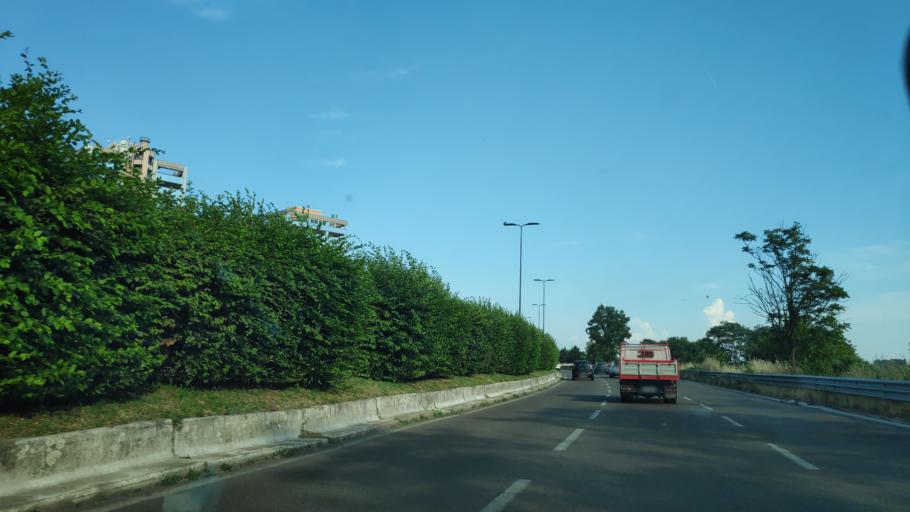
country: IT
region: Lombardy
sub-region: Citta metropolitana di Milano
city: Noverasco-Sporting Mirasole
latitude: 45.4228
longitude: 9.1985
